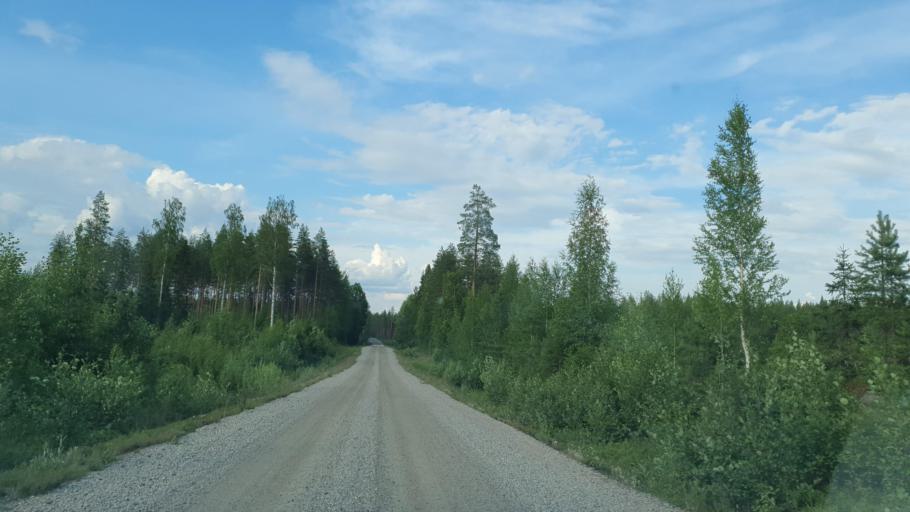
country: FI
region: Kainuu
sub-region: Kehys-Kainuu
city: Kuhmo
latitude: 64.2829
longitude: 29.4592
